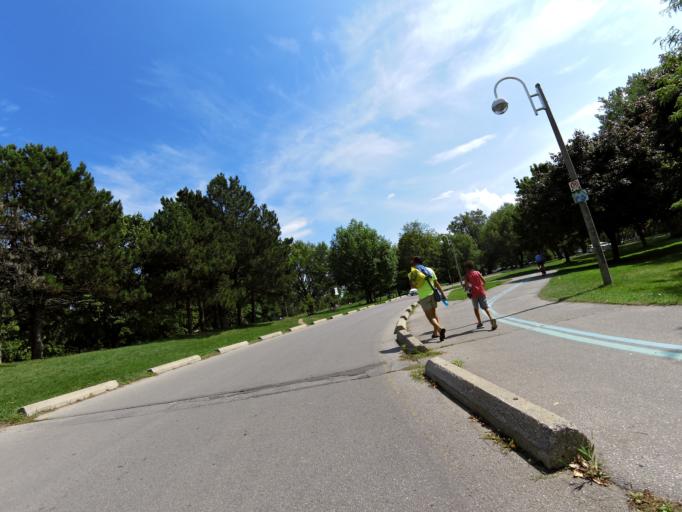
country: CA
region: Ontario
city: Toronto
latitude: 43.6619
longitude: -79.3129
